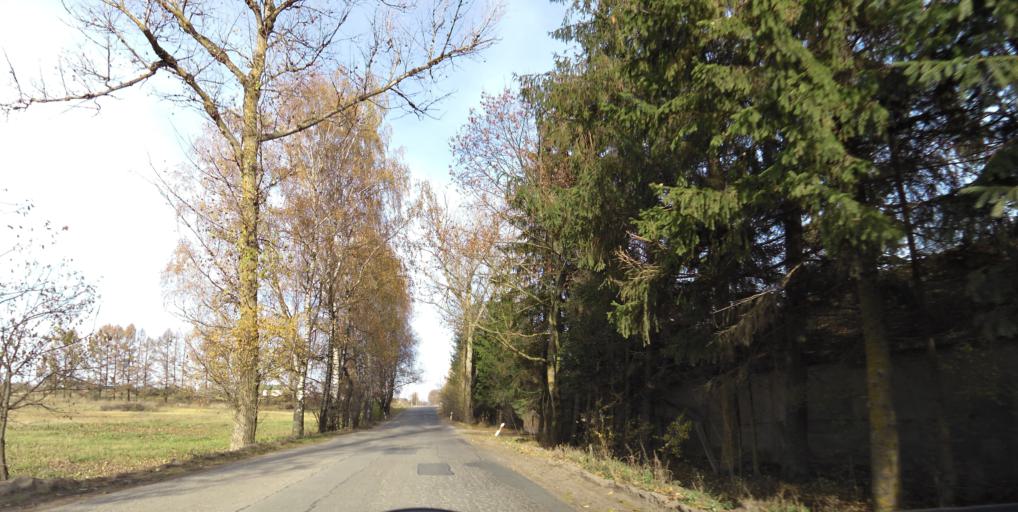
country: LT
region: Vilnius County
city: Pilaite
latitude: 54.7150
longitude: 25.1597
